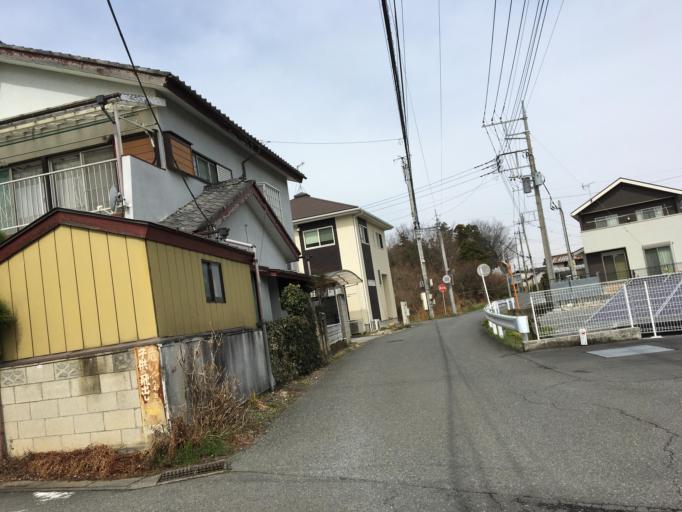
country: JP
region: Saitama
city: Yorii
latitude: 36.1269
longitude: 139.2213
